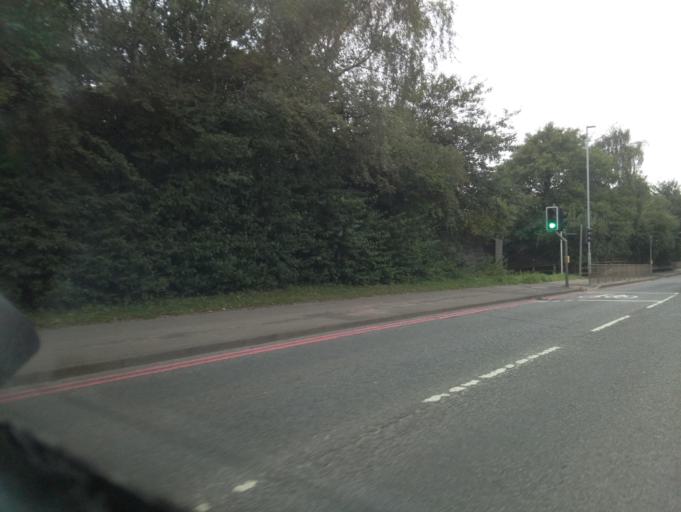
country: GB
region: England
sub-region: Stoke-on-Trent
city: Stoke-on-Trent
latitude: 53.0034
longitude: -2.1766
